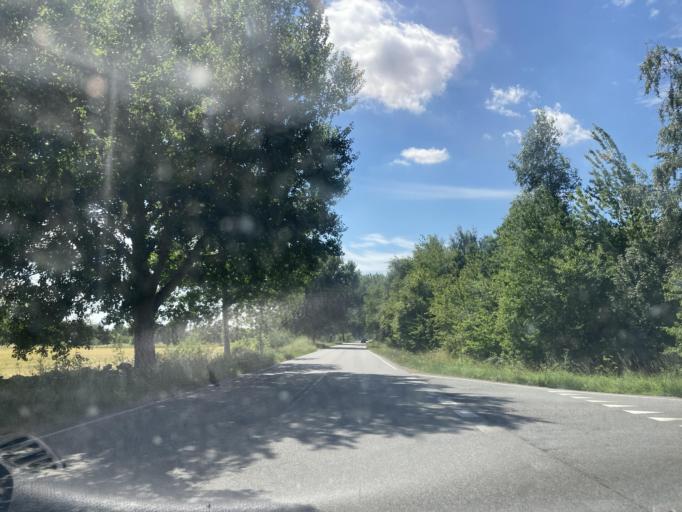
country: DK
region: Zealand
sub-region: Koge Kommune
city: Ejby
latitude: 55.4919
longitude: 12.0946
